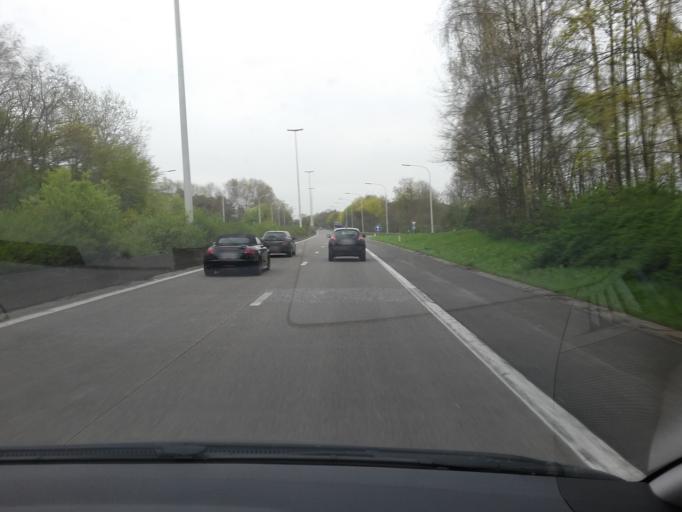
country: BE
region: Wallonia
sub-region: Province du Brabant Wallon
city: Genappe
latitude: 50.6185
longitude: 4.4690
